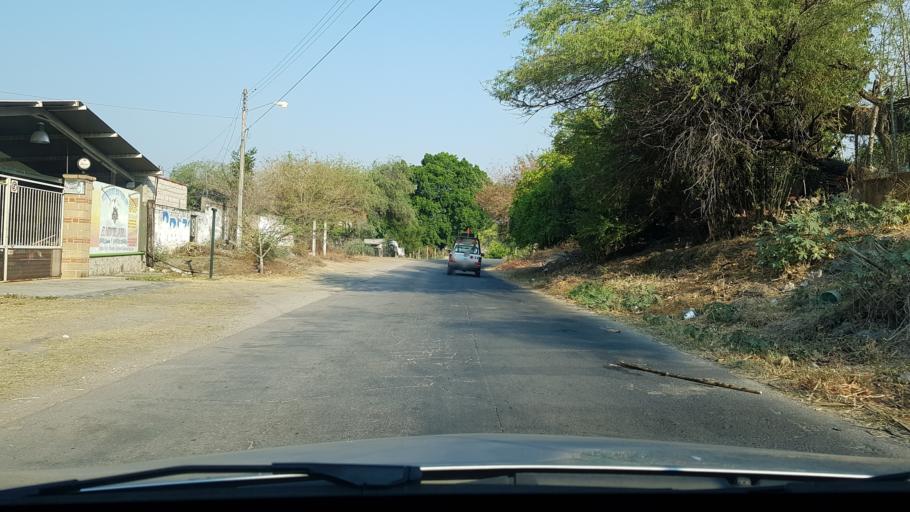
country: MX
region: Morelos
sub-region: Tlaltizapan de Zapata
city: Colonia Palo Prieto (Chipitongo)
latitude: 18.6964
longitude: -99.1025
